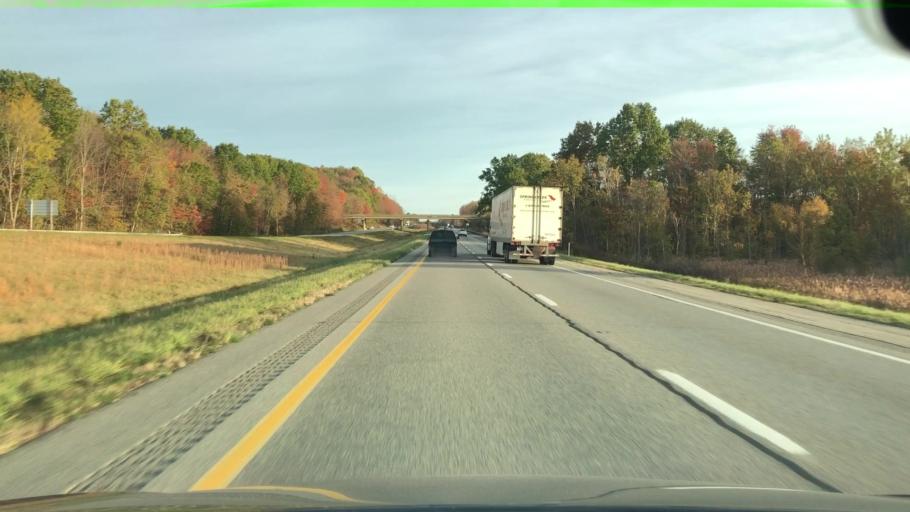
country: US
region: Pennsylvania
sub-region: Mercer County
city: Stoneboro
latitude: 41.2921
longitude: -80.1578
